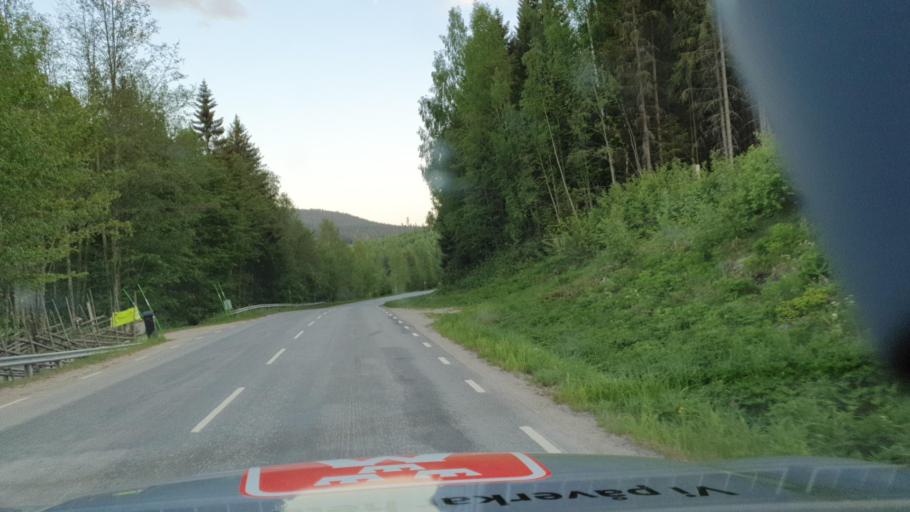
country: SE
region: Vaesternorrland
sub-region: OErnskoeldsviks Kommun
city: Ornskoldsvik
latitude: 63.2419
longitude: 18.6573
